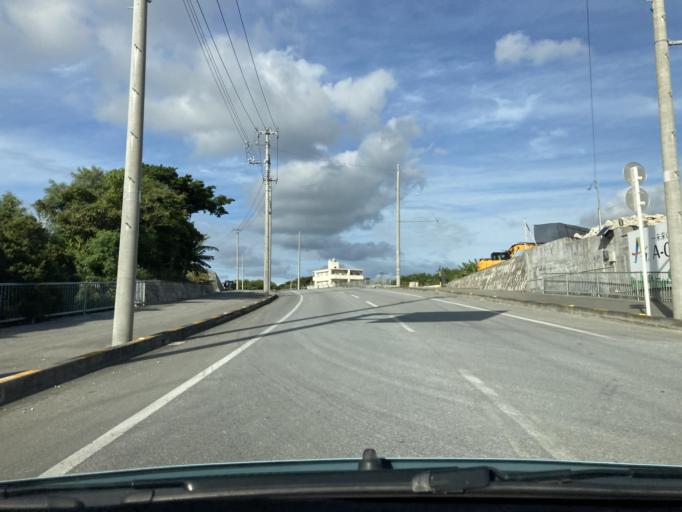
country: JP
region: Okinawa
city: Itoman
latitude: 26.1288
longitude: 127.6834
